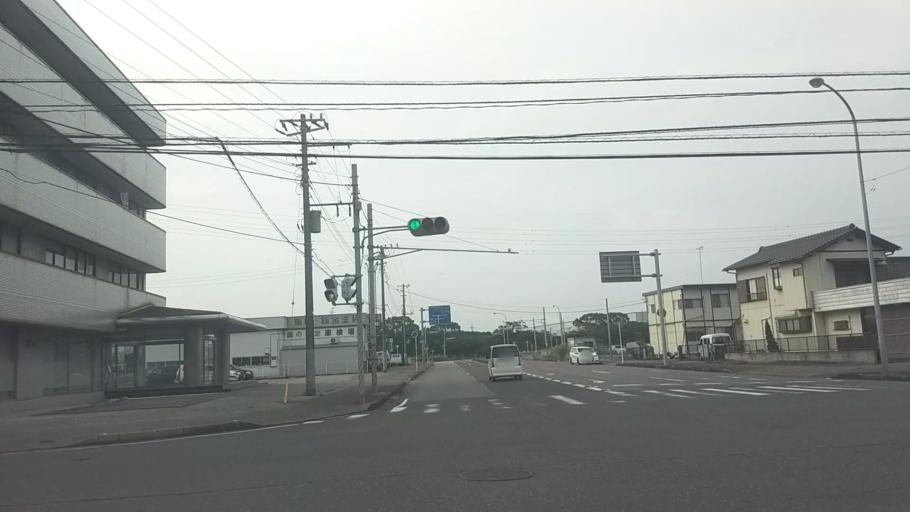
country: JP
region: Chiba
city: Kimitsu
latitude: 35.3462
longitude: 139.8902
